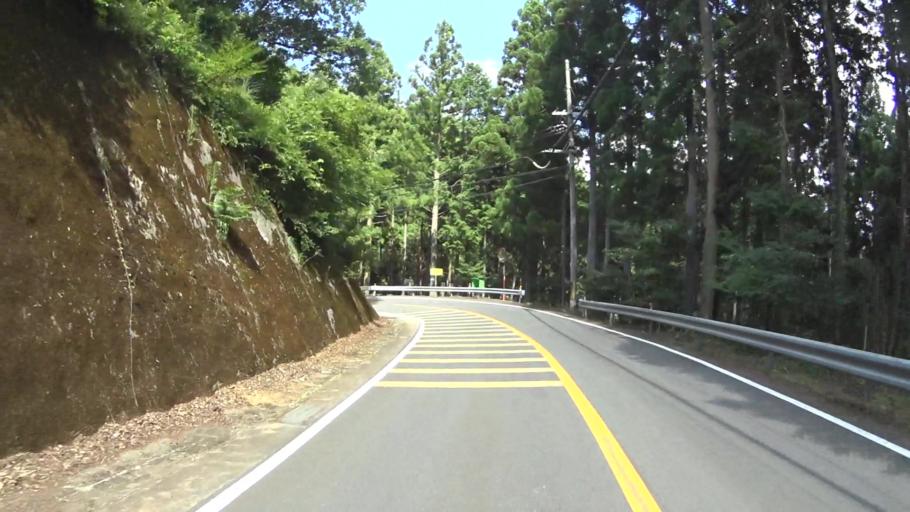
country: JP
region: Kyoto
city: Kameoka
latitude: 35.2760
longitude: 135.5721
